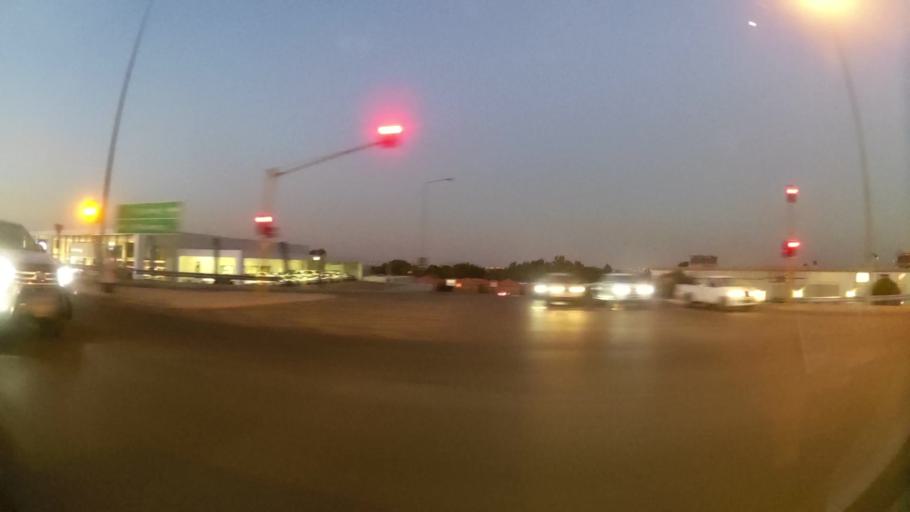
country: ZA
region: North-West
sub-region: Bojanala Platinum District Municipality
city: Rustenburg
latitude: -25.6945
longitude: 27.2535
